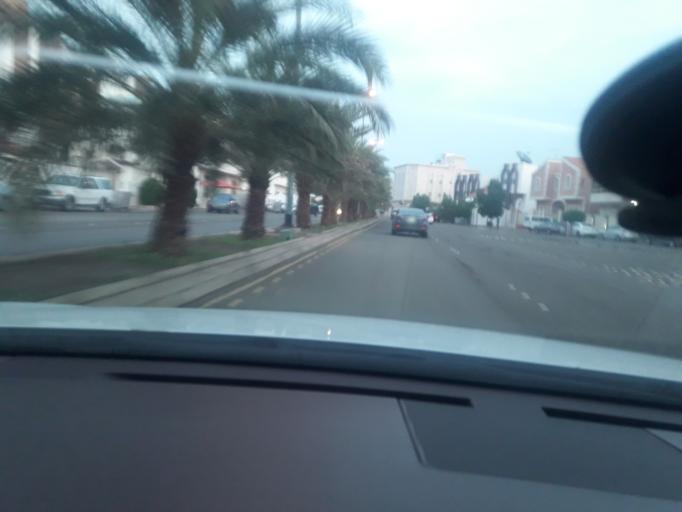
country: SA
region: Al Madinah al Munawwarah
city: Sultanah
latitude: 24.4940
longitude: 39.5834
